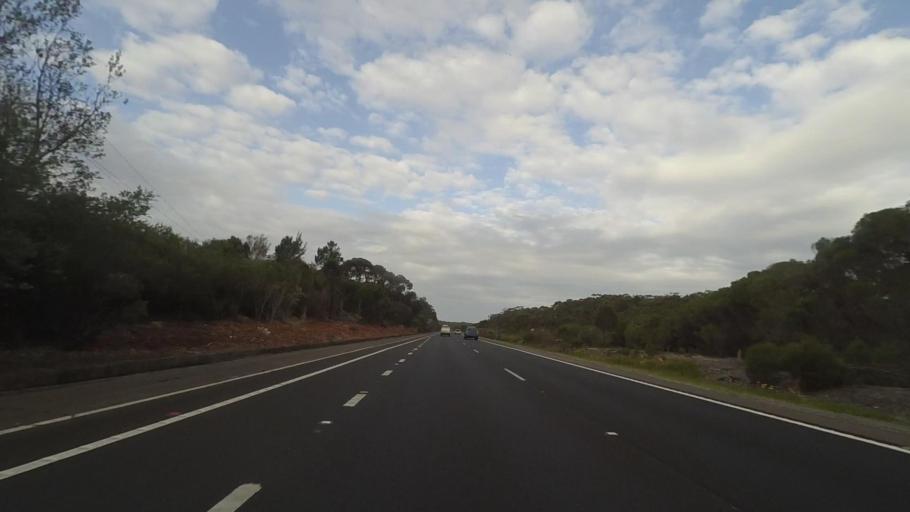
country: AU
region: New South Wales
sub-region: Wollongong
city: Bulli
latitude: -34.2935
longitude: 150.9198
